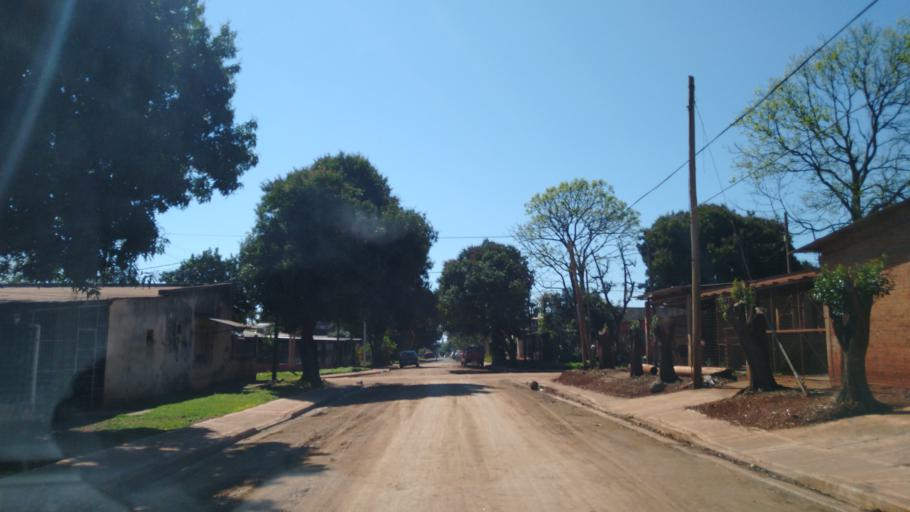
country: AR
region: Misiones
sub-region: Departamento de Capital
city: Posadas
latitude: -27.3866
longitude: -55.9212
